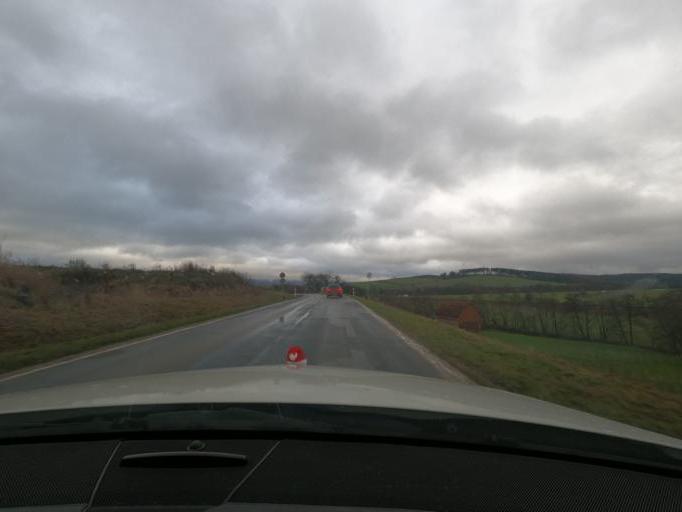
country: DE
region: Lower Saxony
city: Seesen
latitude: 51.8454
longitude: 10.1081
